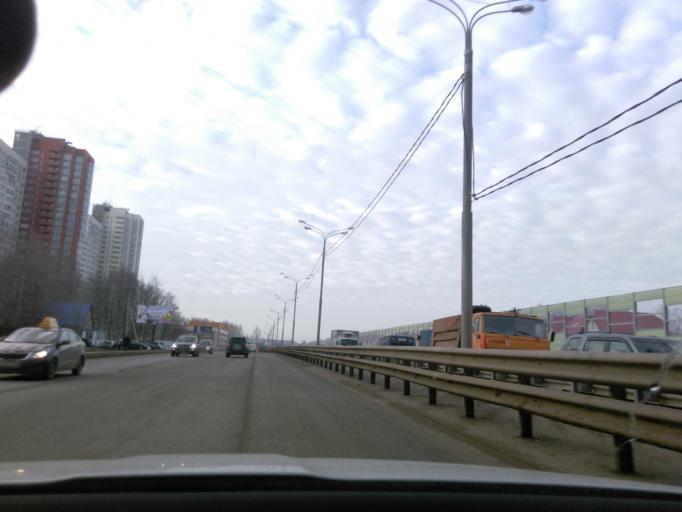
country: RU
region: Moskovskaya
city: Dolgoprudnyy
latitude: 55.9349
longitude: 37.4924
